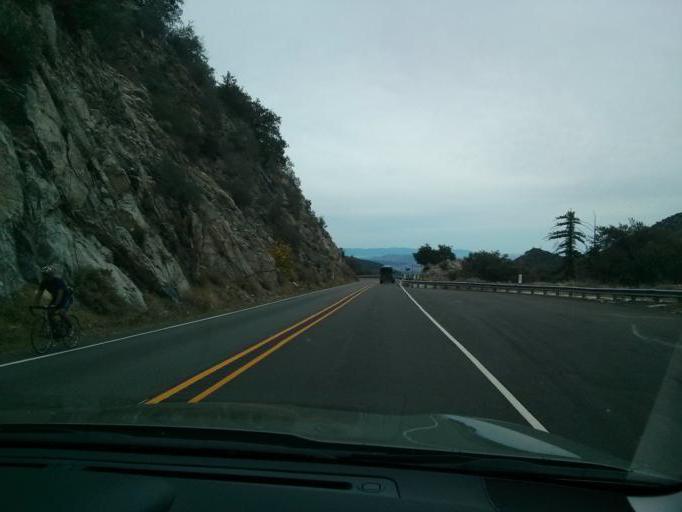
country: US
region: California
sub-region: San Bernardino County
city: Yucaipa
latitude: 34.1154
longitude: -116.9794
